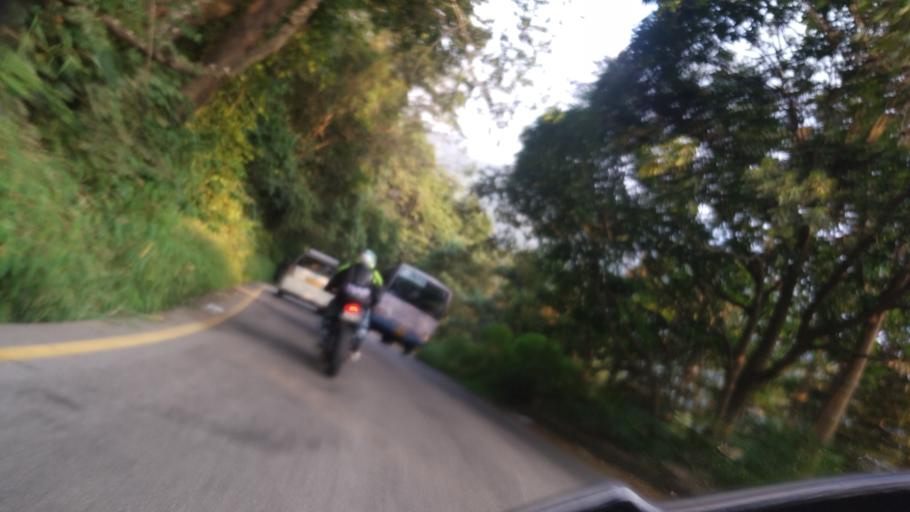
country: IN
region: Kerala
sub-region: Wayanad
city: Kalpetta
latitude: 11.5101
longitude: 76.0233
